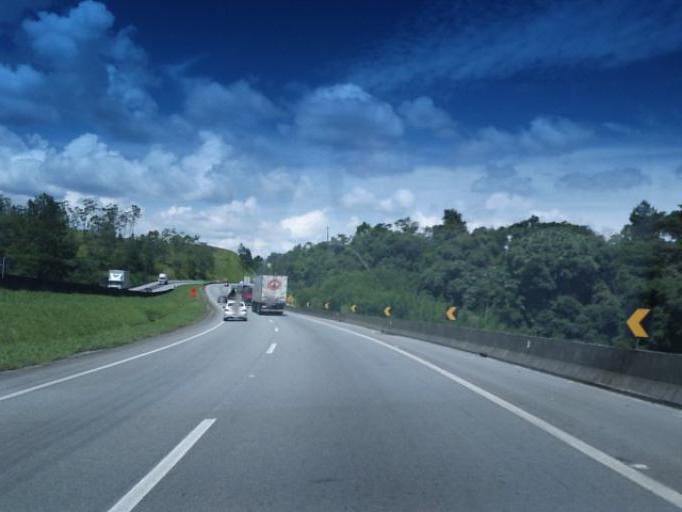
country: BR
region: Sao Paulo
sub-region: Juquitiba
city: Juquitiba
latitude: -23.9352
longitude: -47.0754
